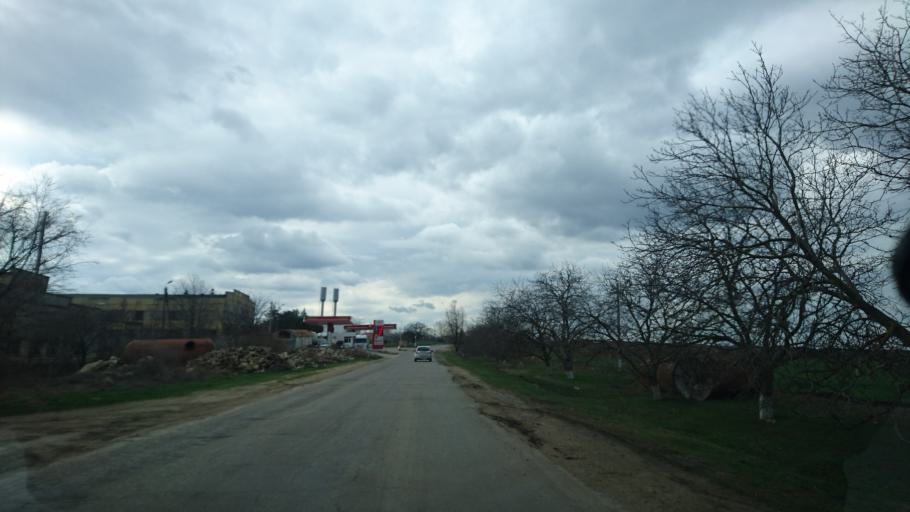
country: MD
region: Gagauzia
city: Comrat
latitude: 46.3044
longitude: 28.6304
